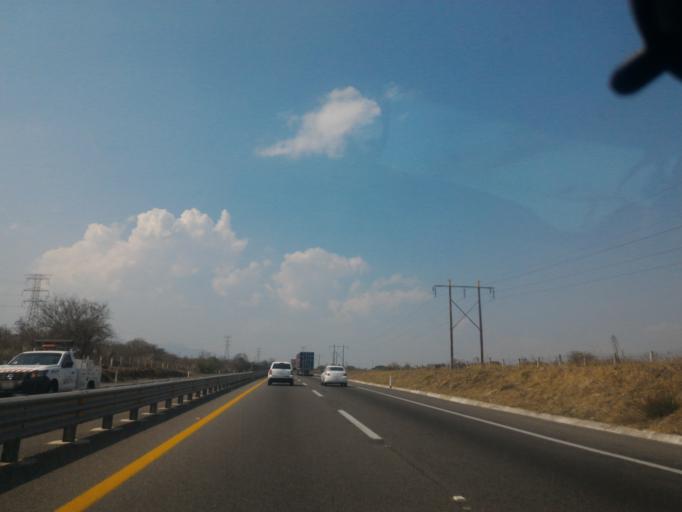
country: MX
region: Jalisco
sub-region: Zapotlan el Grande
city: Ciudad Guzman [CERESO]
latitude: 19.6553
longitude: -103.4803
